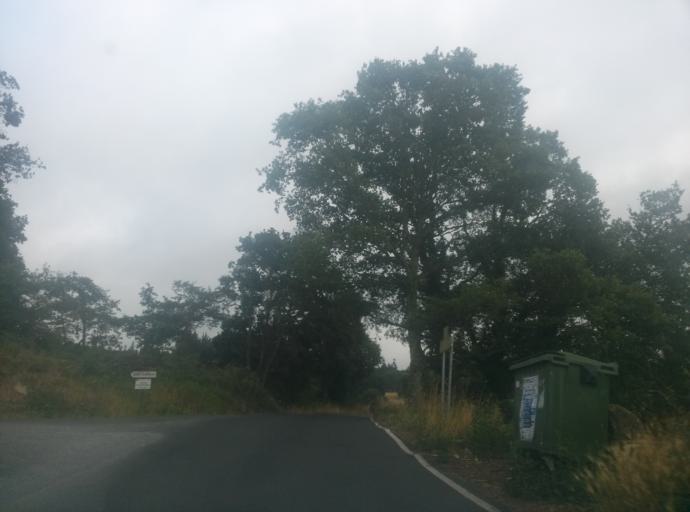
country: ES
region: Galicia
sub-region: Provincia de Lugo
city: Outeiro de Rei
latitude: 43.0813
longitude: -7.5469
